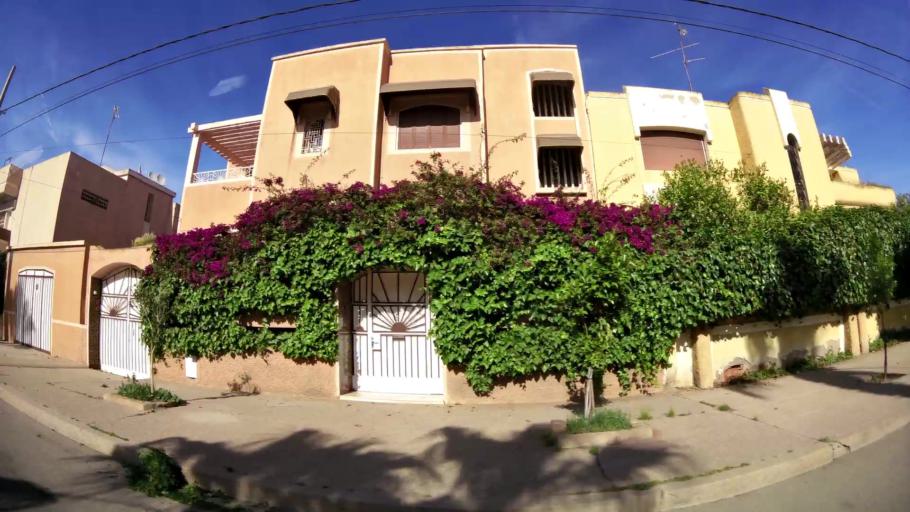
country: MA
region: Oriental
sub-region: Oujda-Angad
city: Oujda
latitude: 34.6630
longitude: -1.8988
